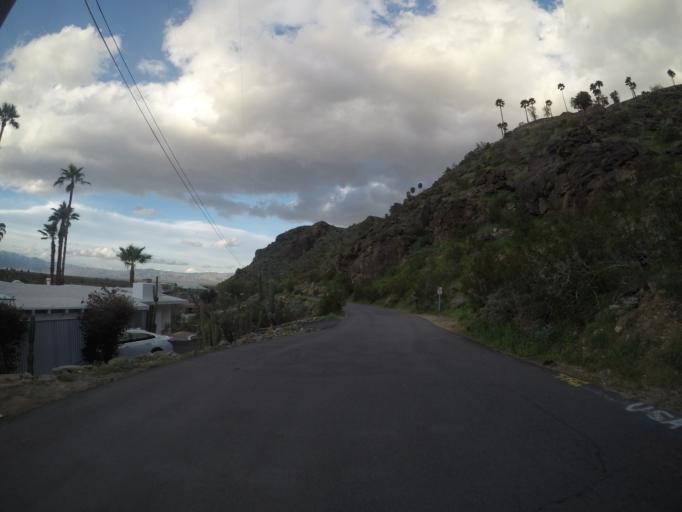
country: US
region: California
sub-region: Riverside County
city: Cathedral City
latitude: 33.7928
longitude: -116.5128
